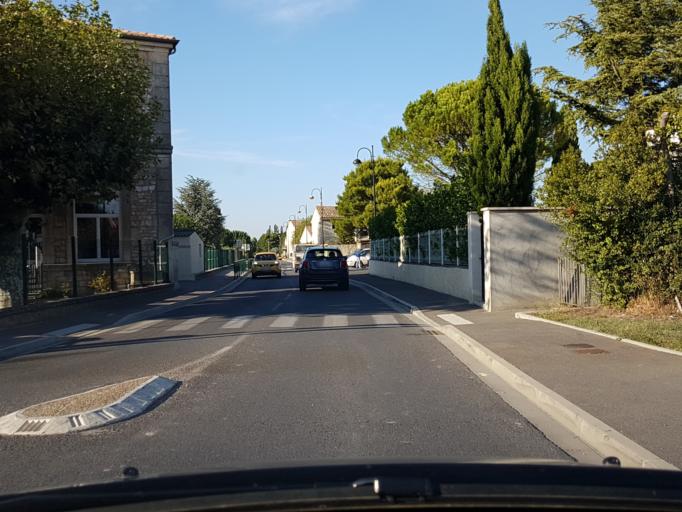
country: FR
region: Provence-Alpes-Cote d'Azur
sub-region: Departement des Bouches-du-Rhone
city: Molleges
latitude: 43.8075
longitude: 4.9490
